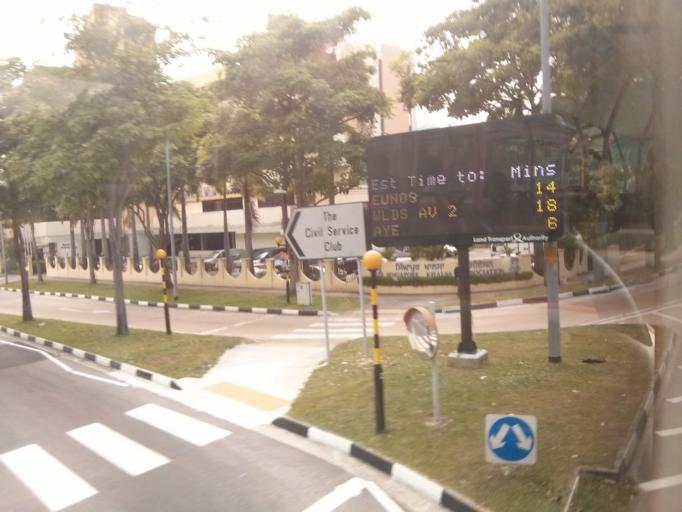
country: SG
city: Singapore
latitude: 1.3167
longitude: 103.8578
